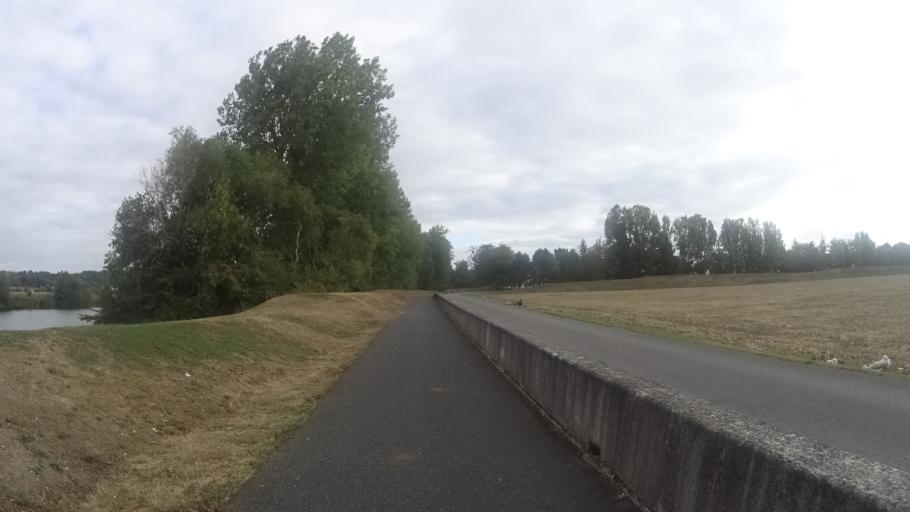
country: FR
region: Picardie
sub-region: Departement de l'Oise
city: Lacroix-Saint-Ouen
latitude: 49.3672
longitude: 2.7705
